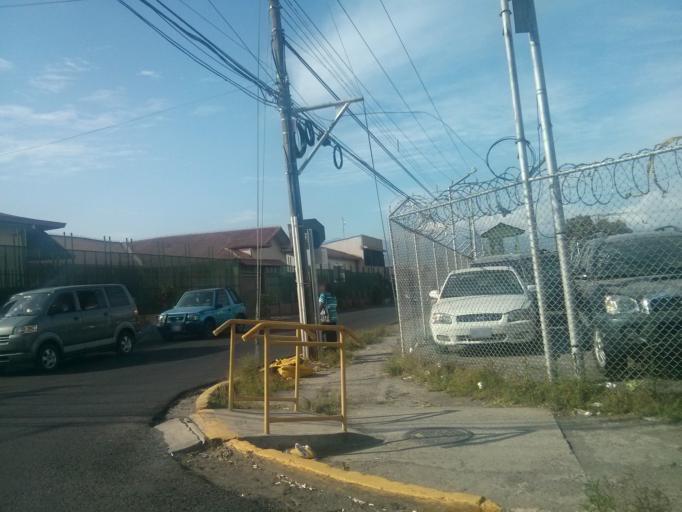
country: CR
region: San Jose
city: Colima
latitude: 9.9467
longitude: -84.0803
